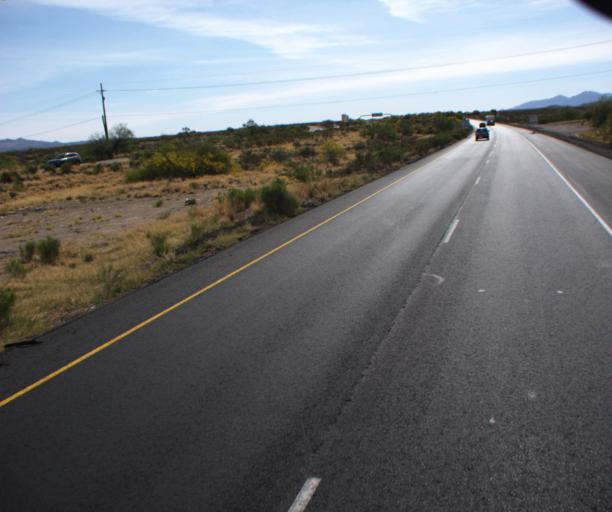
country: US
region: Arizona
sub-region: Pima County
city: Vail
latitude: 32.0026
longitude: -110.6834
